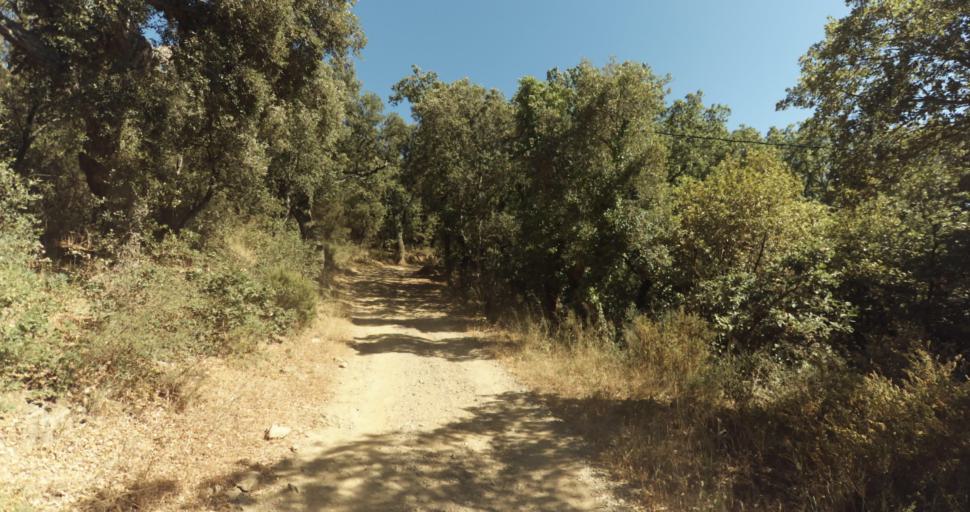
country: FR
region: Provence-Alpes-Cote d'Azur
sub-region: Departement du Var
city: Gassin
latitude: 43.2414
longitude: 6.5838
